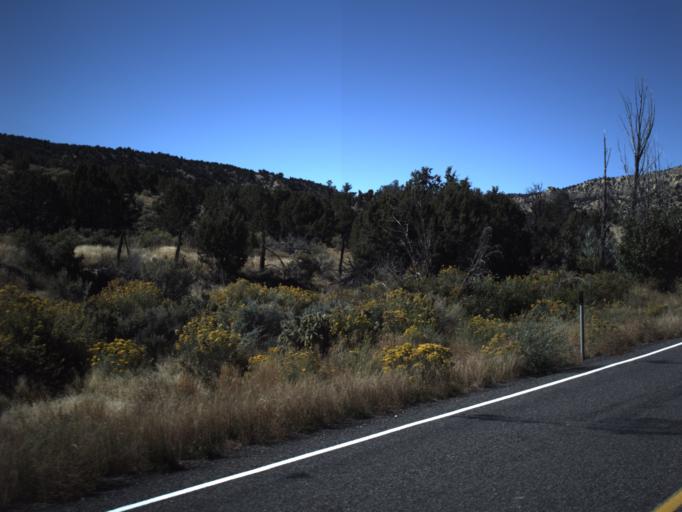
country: US
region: Utah
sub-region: Garfield County
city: Panguitch
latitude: 37.6509
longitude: -112.0817
